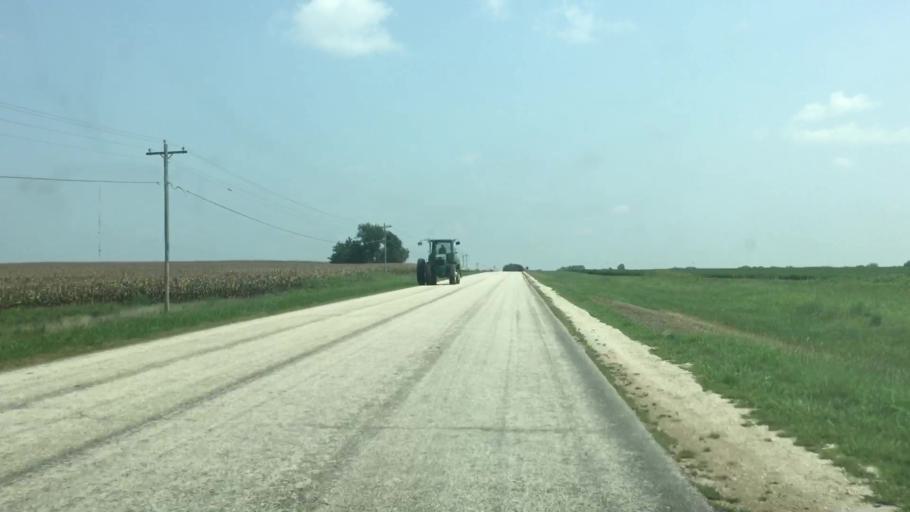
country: US
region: Kansas
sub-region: Allen County
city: Iola
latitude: 37.9512
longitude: -95.3870
